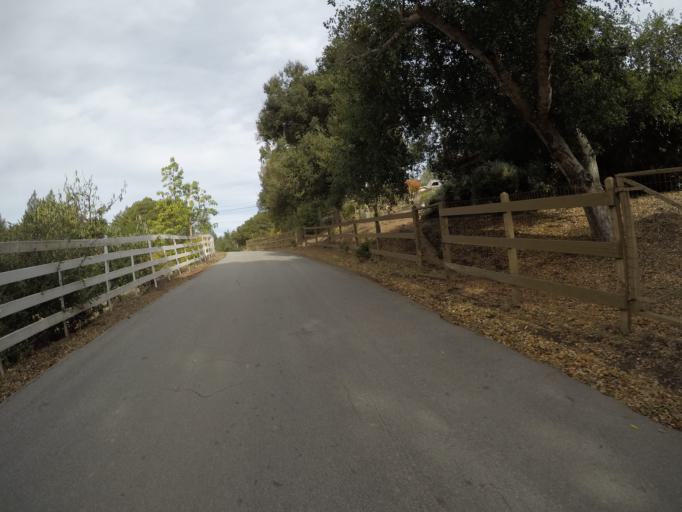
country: US
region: California
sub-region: Santa Cruz County
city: Scotts Valley
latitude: 37.0562
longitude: -121.9914
